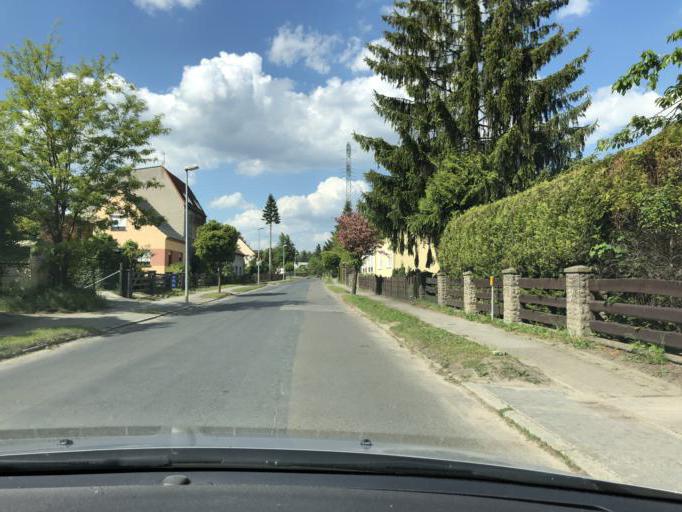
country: DE
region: Brandenburg
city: Rehfelde
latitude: 52.4843
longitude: 13.8482
